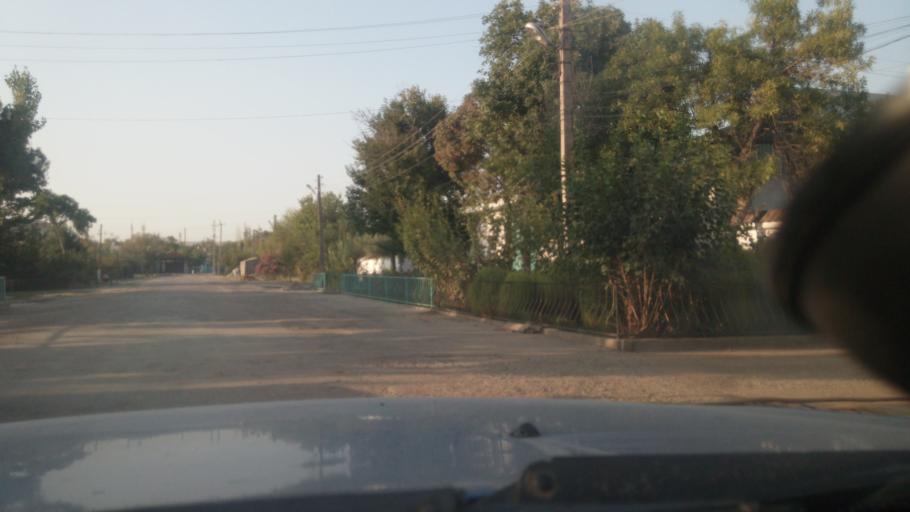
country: UZ
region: Sirdaryo
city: Guliston
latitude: 40.4935
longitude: 68.7851
